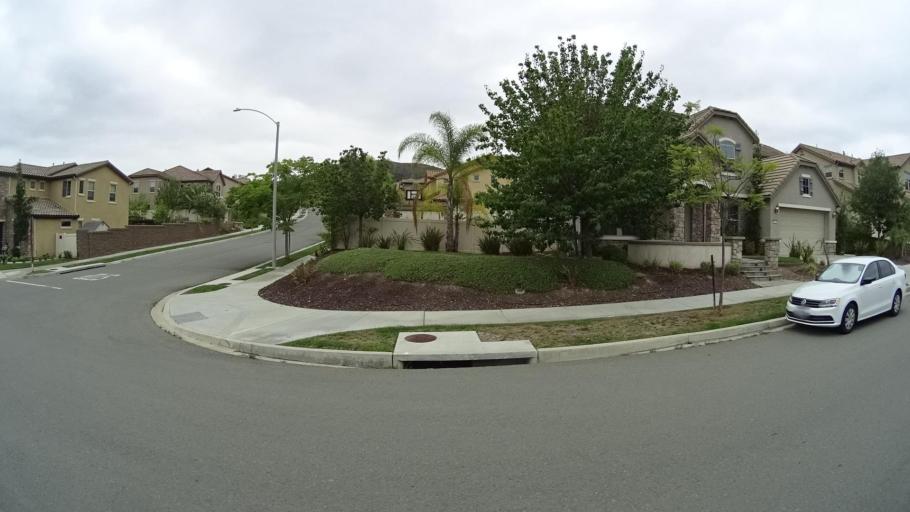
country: US
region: California
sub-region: San Diego County
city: Escondido
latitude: 33.0388
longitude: -117.1142
